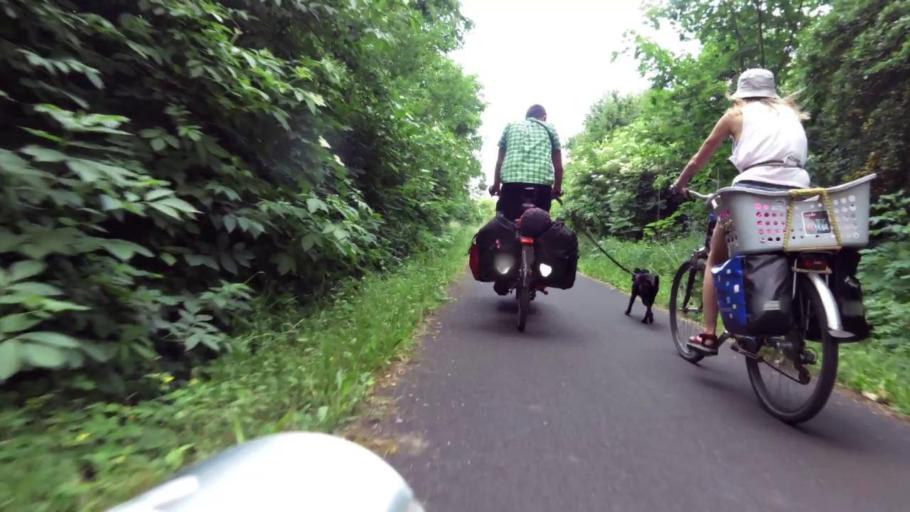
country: PL
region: Kujawsko-Pomorskie
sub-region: Powiat torunski
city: Lubianka
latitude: 53.0944
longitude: 18.5323
